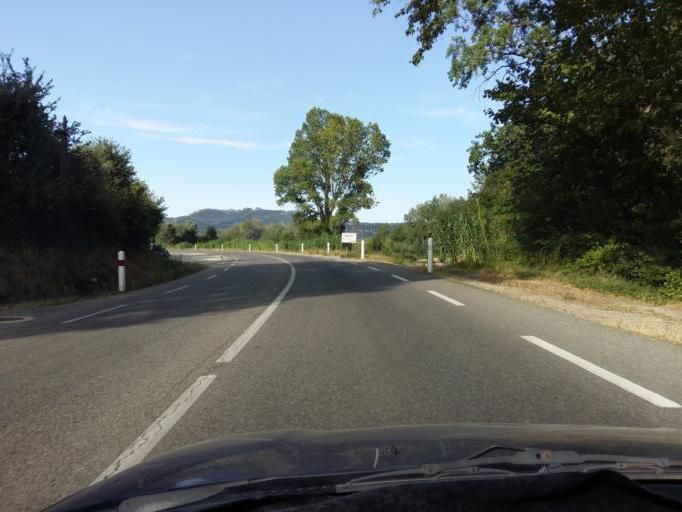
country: FR
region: Provence-Alpes-Cote d'Azur
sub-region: Departement du Vaucluse
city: Sarrians
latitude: 44.0966
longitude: 4.9836
